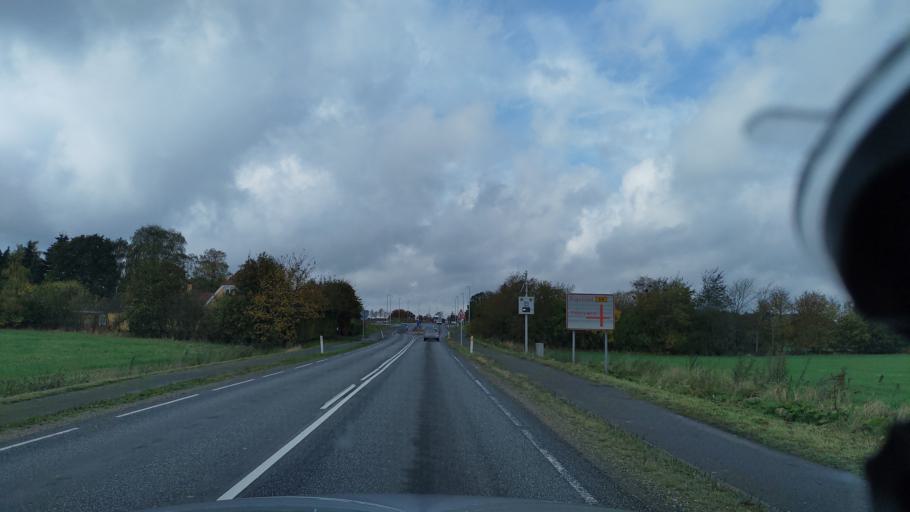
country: DK
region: Zealand
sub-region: Naestved Kommune
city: Fensmark
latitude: 55.2581
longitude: 11.8897
